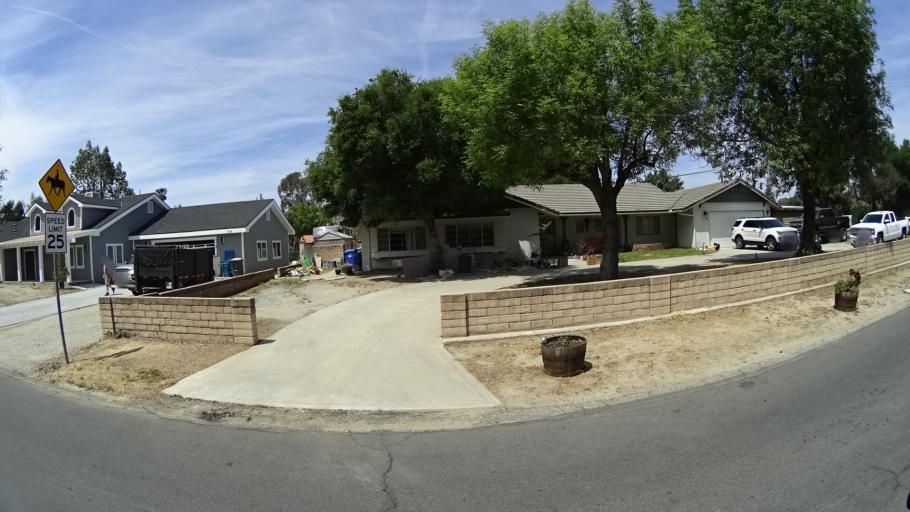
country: US
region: California
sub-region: Ventura County
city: Thousand Oaks
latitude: 34.1990
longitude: -118.8644
